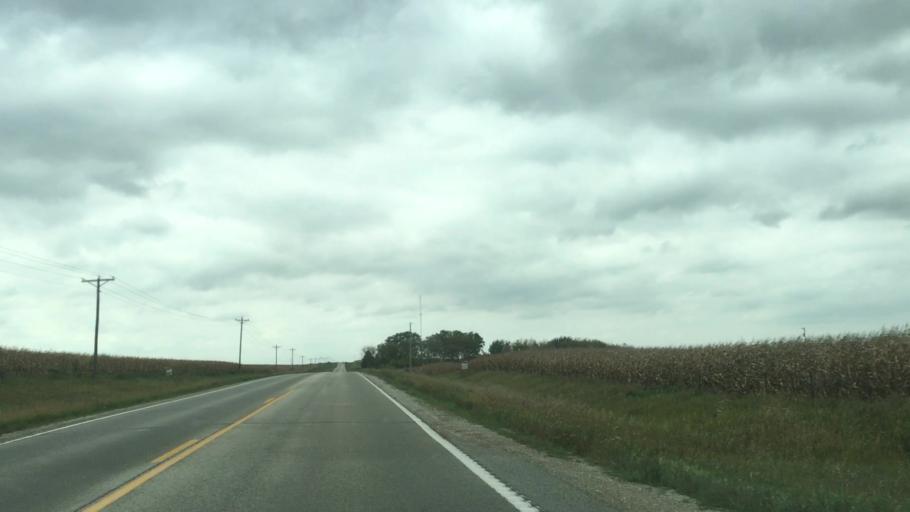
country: US
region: Minnesota
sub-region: Fillmore County
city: Preston
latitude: 43.7319
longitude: -92.0646
